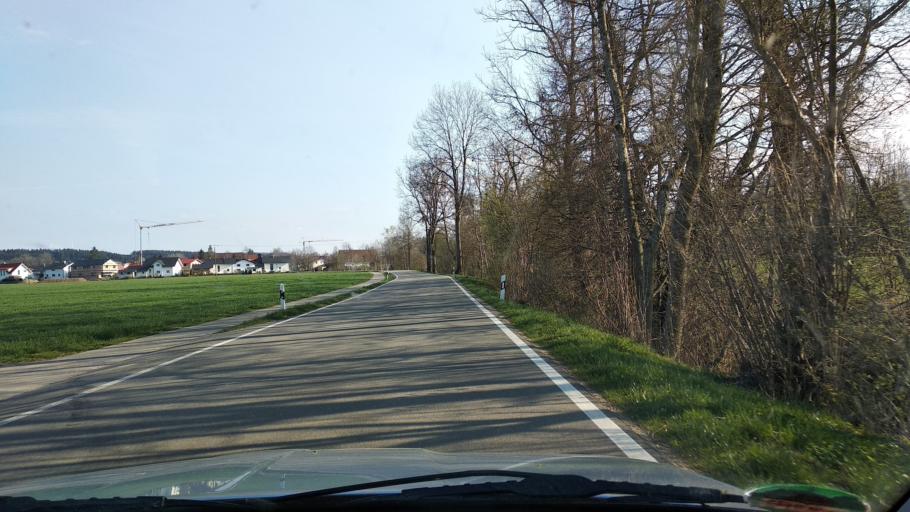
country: DE
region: Bavaria
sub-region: Swabia
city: Legau
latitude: 47.8314
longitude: 10.0966
